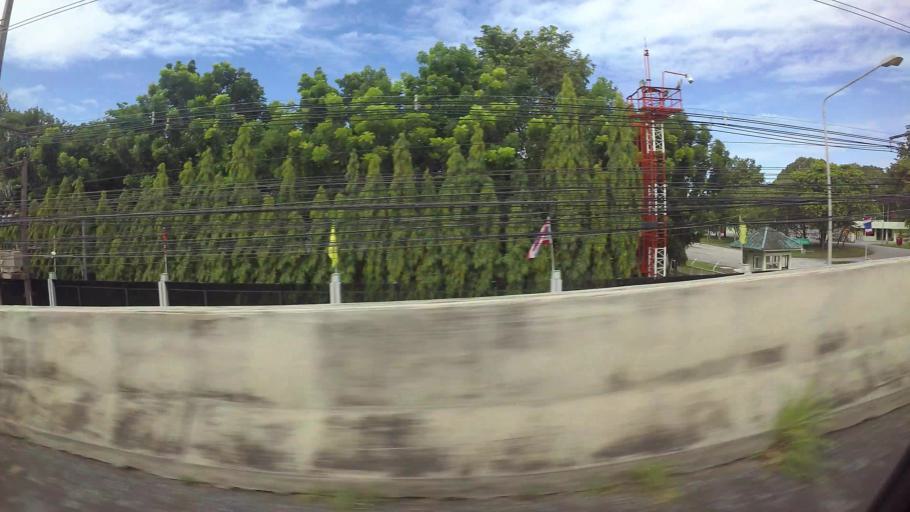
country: TH
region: Rayong
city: Ban Chang
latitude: 12.7259
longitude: 101.1468
